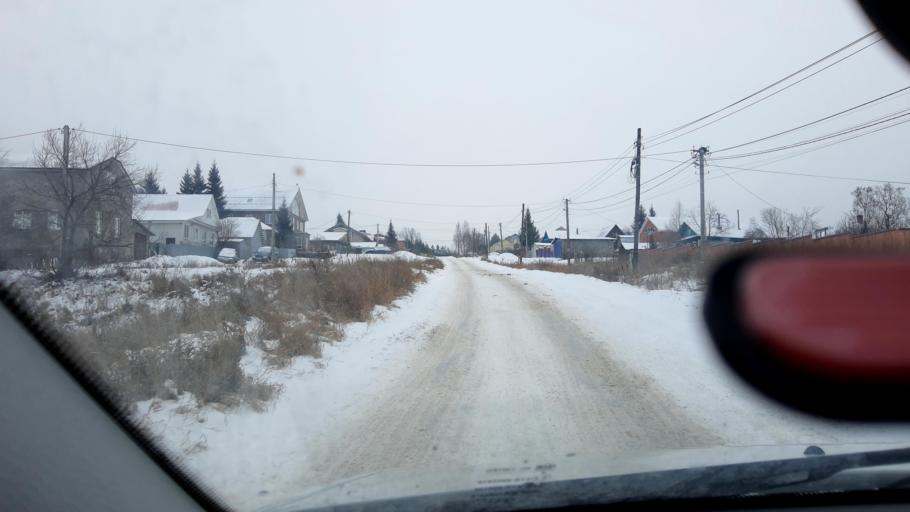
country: RU
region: Bashkortostan
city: Kabakovo
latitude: 54.6369
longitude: 56.0812
